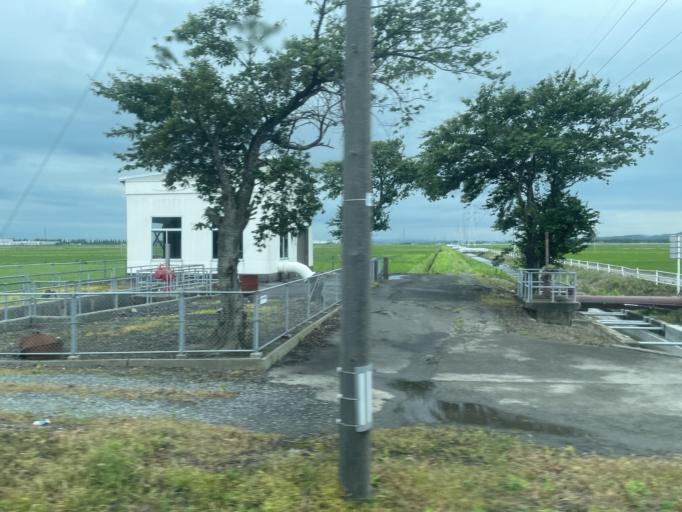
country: JP
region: Niigata
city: Yoshida-kasugacho
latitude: 37.6866
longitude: 138.8617
